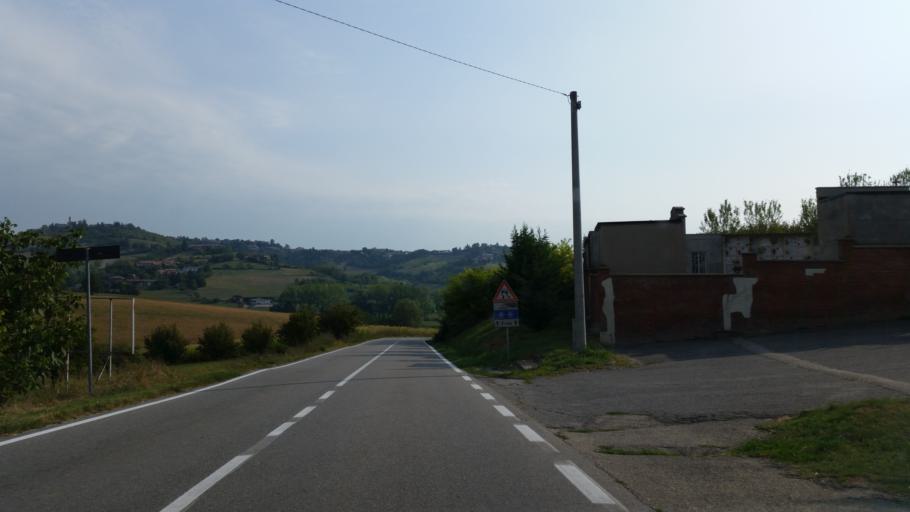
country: IT
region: Piedmont
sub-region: Provincia di Asti
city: Robella
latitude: 45.0845
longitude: 8.0883
